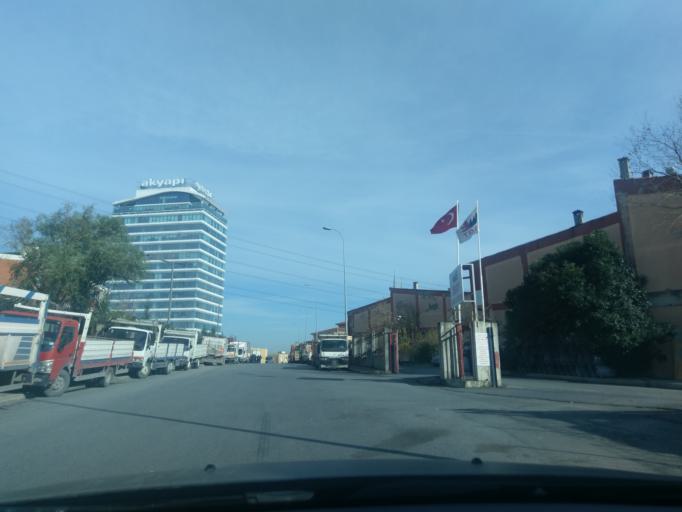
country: TR
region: Istanbul
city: Basaksehir
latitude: 41.0679
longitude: 28.8028
